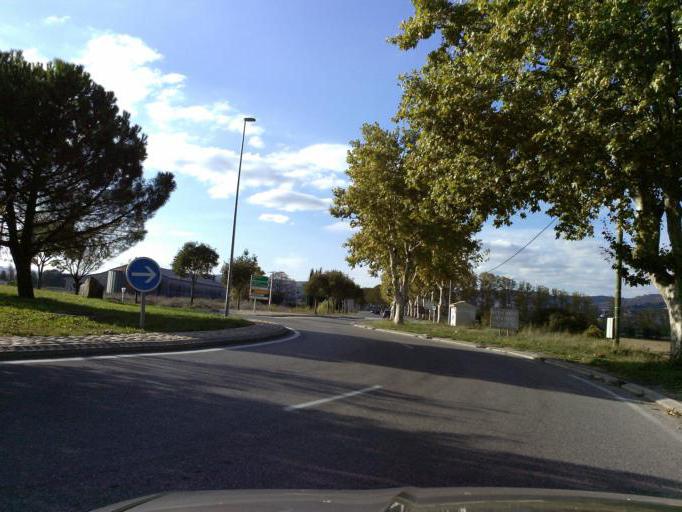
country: FR
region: Provence-Alpes-Cote d'Azur
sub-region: Departement des Alpes-de-Haute-Provence
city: Manosque
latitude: 43.8099
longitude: 5.8125
